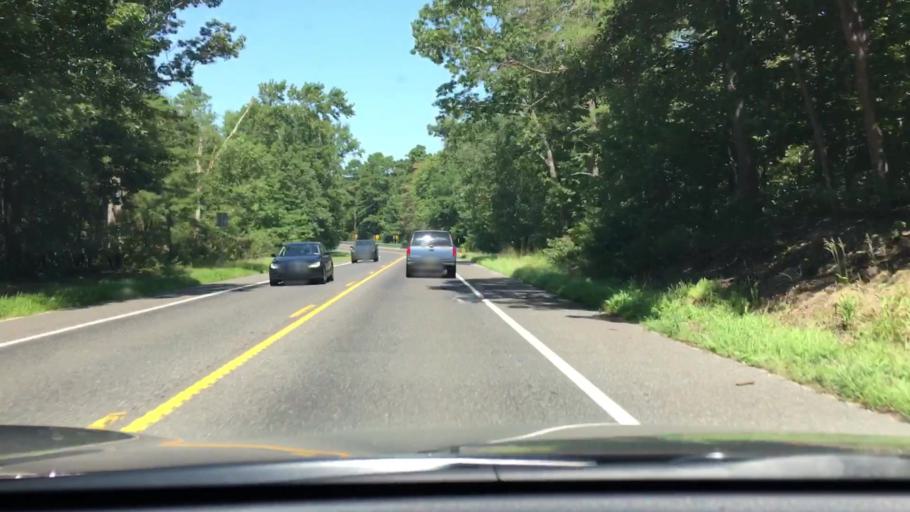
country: US
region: New Jersey
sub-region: Cumberland County
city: Port Norris
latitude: 39.2835
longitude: -74.9511
